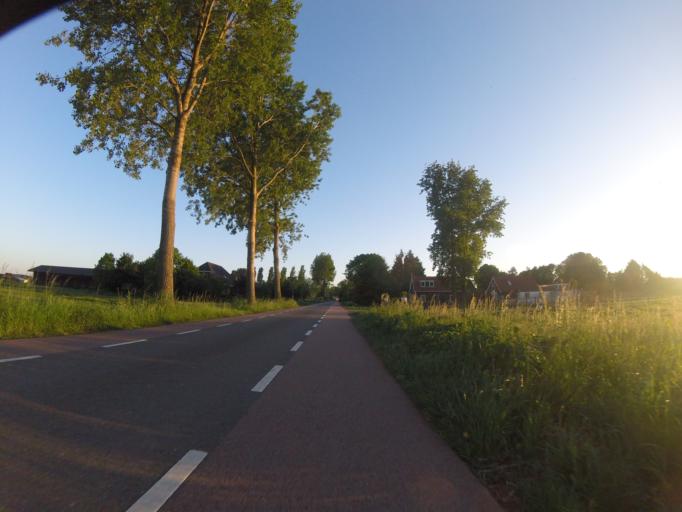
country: NL
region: North Holland
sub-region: Gemeente Haarlemmermeer
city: Hoofddorp
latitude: 52.3607
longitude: 4.6924
